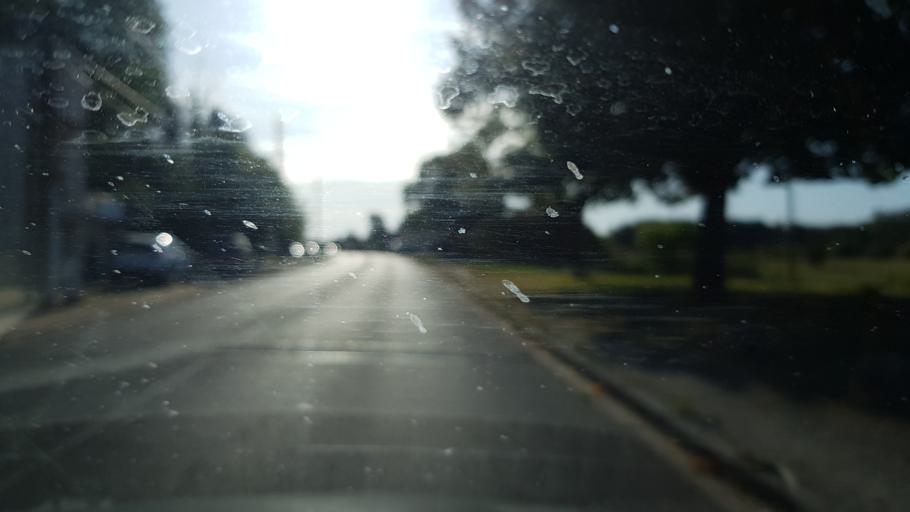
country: FR
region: Centre
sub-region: Departement du Loiret
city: Saint-Martin-sur-Ocre
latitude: 47.6780
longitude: 2.6480
